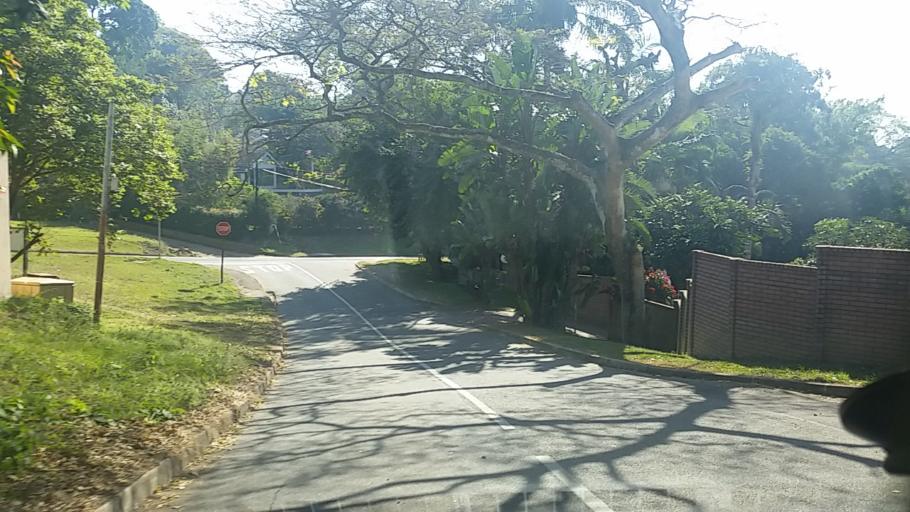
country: ZA
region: KwaZulu-Natal
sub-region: eThekwini Metropolitan Municipality
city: Berea
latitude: -29.8394
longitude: 30.9077
